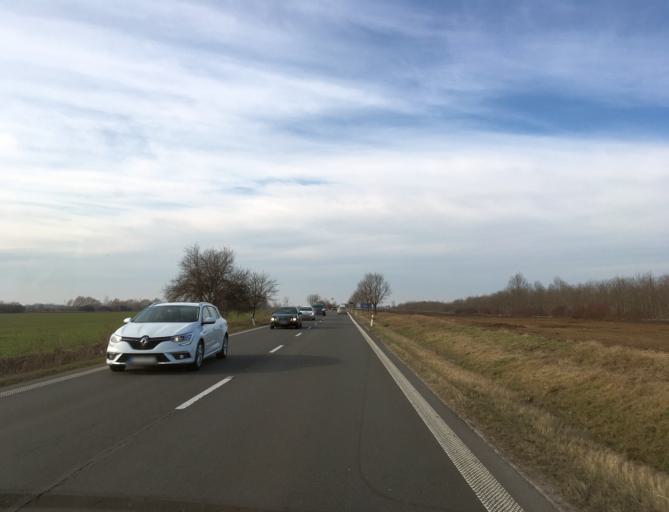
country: SK
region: Nitriansky
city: Surany
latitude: 48.0716
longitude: 18.0899
